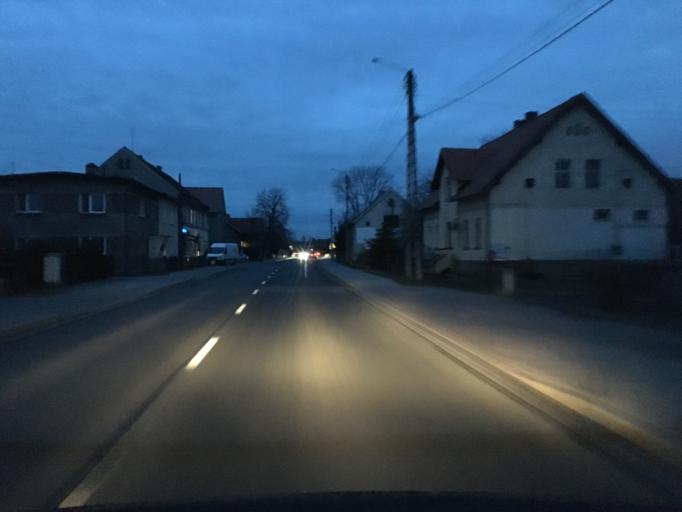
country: PL
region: Opole Voivodeship
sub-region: Powiat brzeski
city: Losiow
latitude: 50.7896
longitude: 17.5704
